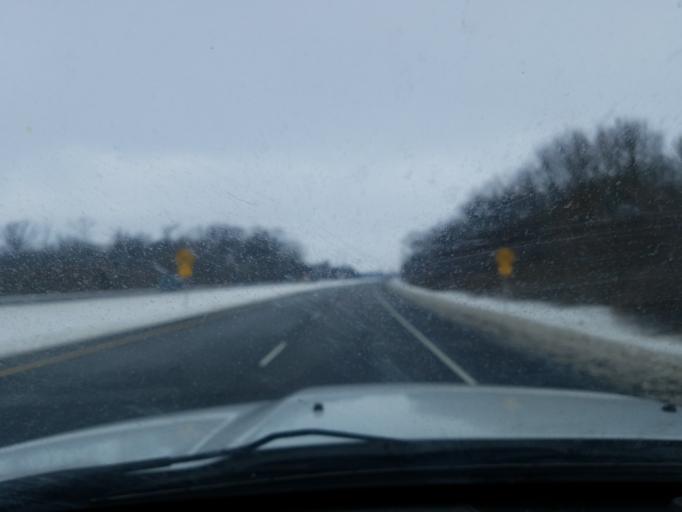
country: US
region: Indiana
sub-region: Marshall County
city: Argos
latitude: 41.2781
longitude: -86.2714
